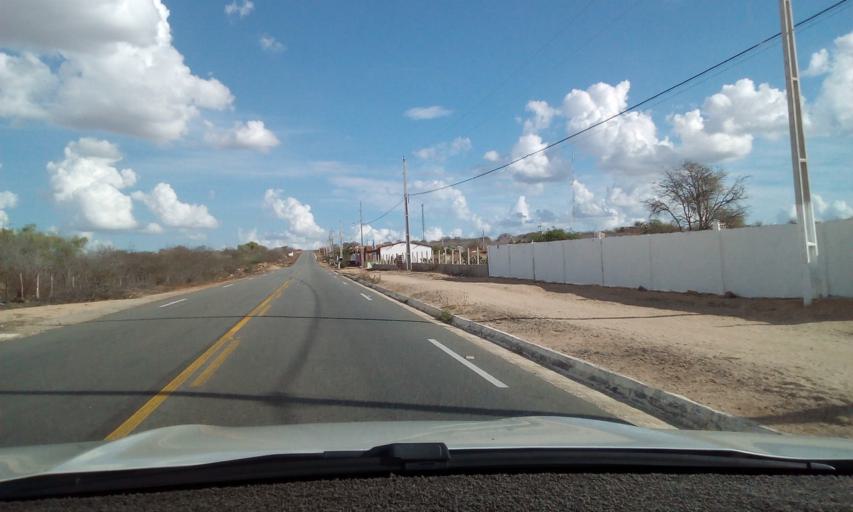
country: BR
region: Paraiba
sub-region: Soledade
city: Soledade
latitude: -6.8601
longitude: -36.4065
